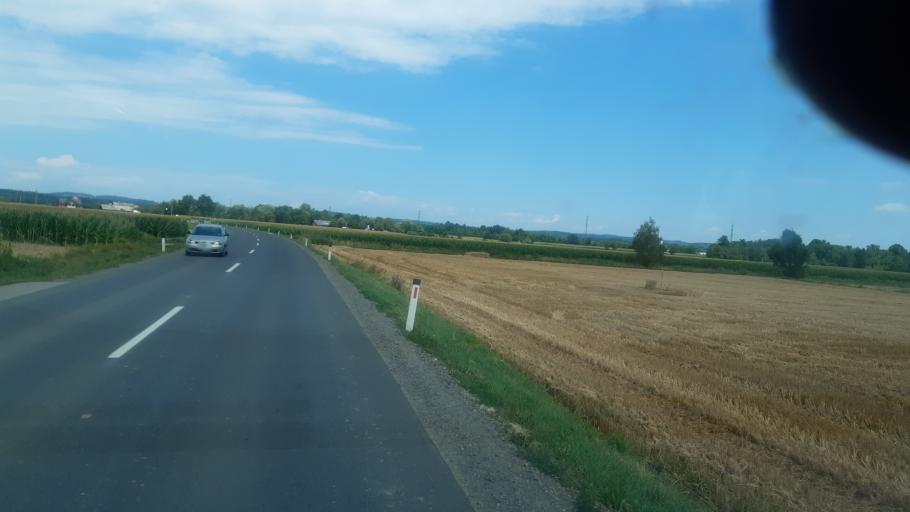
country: SI
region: Murska Sobota
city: Murska Sobota
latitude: 46.6756
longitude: 16.1796
